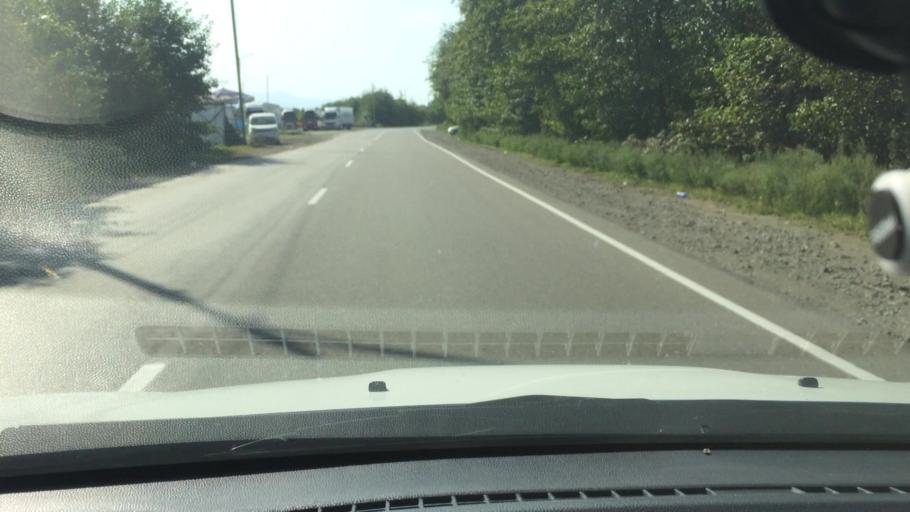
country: GE
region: Guria
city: Urek'i
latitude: 41.9608
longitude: 41.7729
